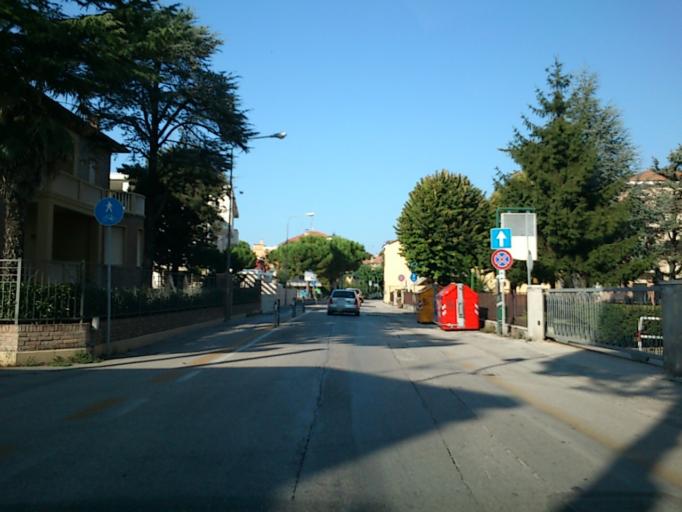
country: IT
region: The Marches
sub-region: Provincia di Pesaro e Urbino
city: Fano
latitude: 43.8381
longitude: 13.0141
